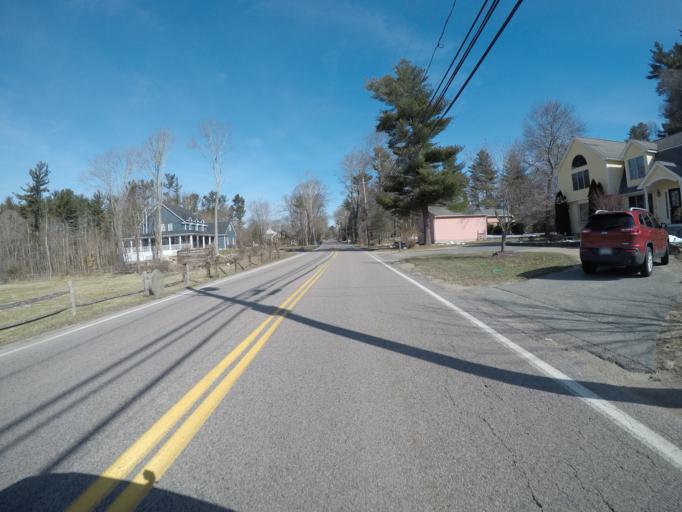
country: US
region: Massachusetts
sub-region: Bristol County
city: Easton
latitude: 42.0164
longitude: -71.1206
